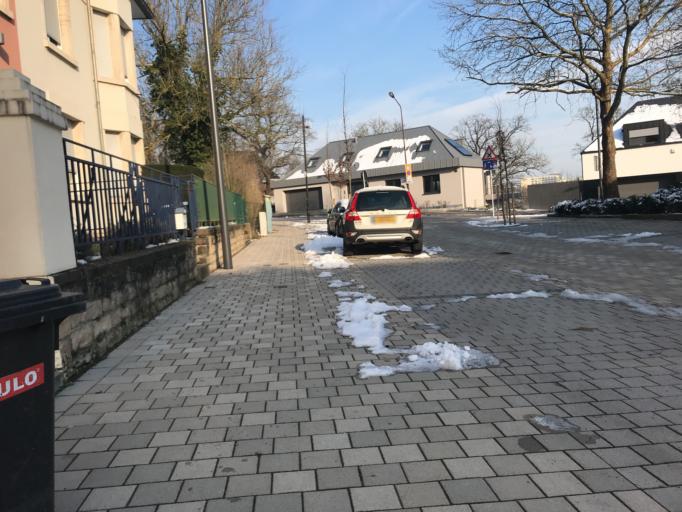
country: LU
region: Luxembourg
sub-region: Canton de Luxembourg
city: Luxembourg
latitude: 49.6034
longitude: 6.1414
